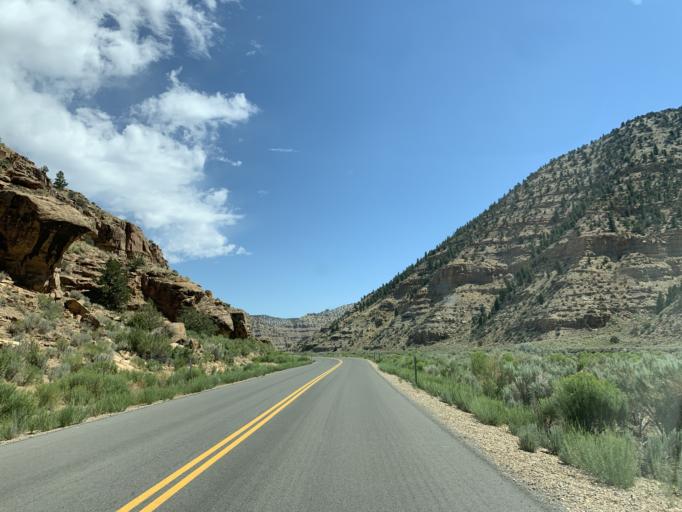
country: US
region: Utah
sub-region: Carbon County
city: East Carbon City
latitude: 39.7863
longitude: -110.3963
